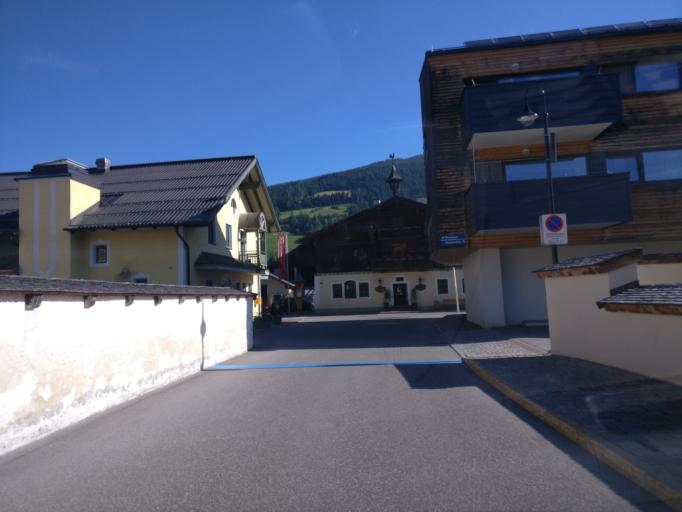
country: AT
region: Salzburg
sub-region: Politischer Bezirk Sankt Johann im Pongau
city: Altenmarkt im Pongau
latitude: 47.3778
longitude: 13.4245
